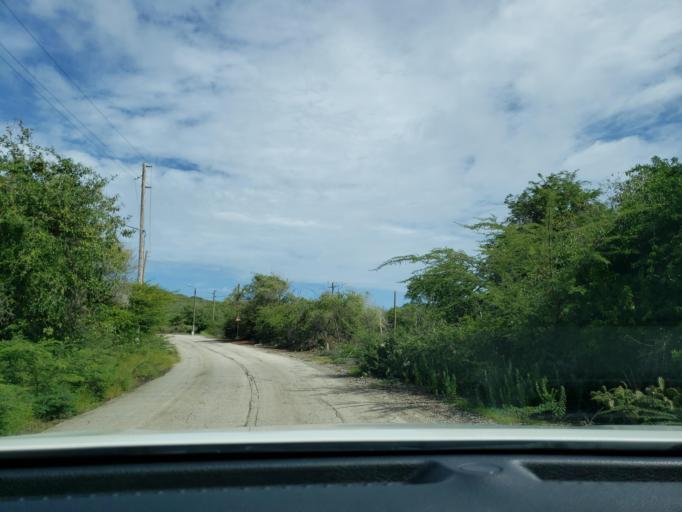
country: CW
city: Barber
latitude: 12.3071
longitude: -69.0896
